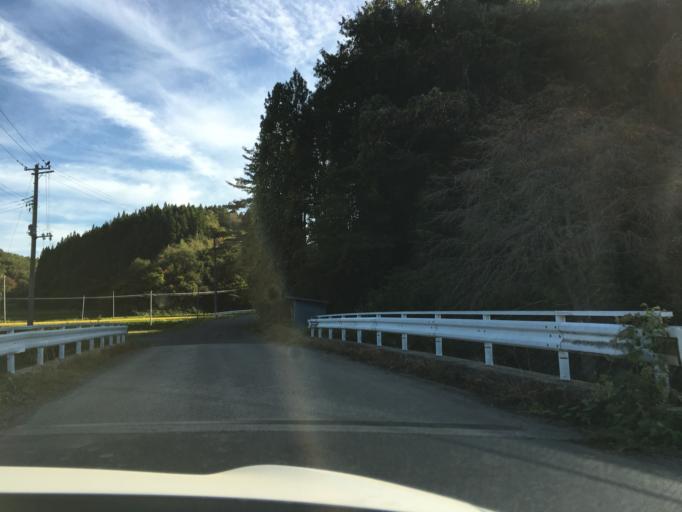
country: JP
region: Fukushima
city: Funehikimachi-funehiki
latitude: 37.2629
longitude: 140.6091
